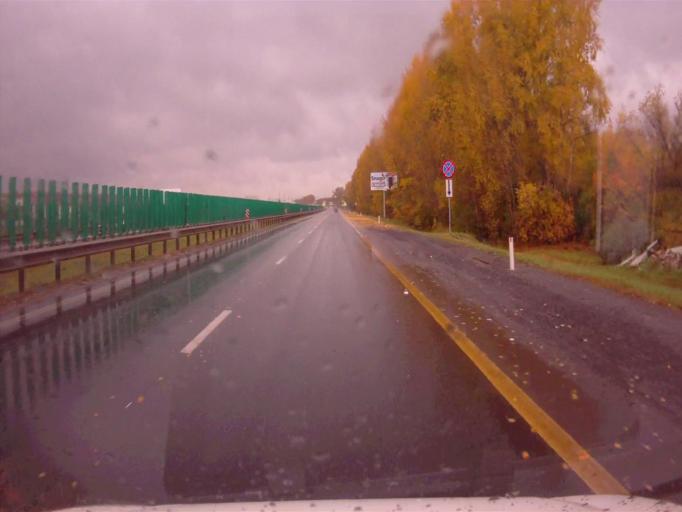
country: RU
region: Chelyabinsk
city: Dolgoderevenskoye
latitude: 55.2792
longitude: 61.3434
